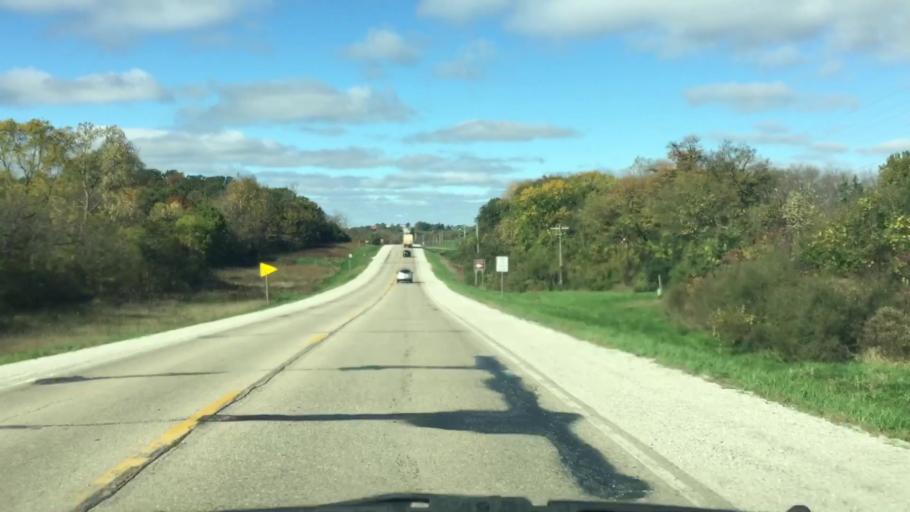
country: US
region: Iowa
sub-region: Decatur County
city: Leon
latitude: 40.7400
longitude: -93.7683
